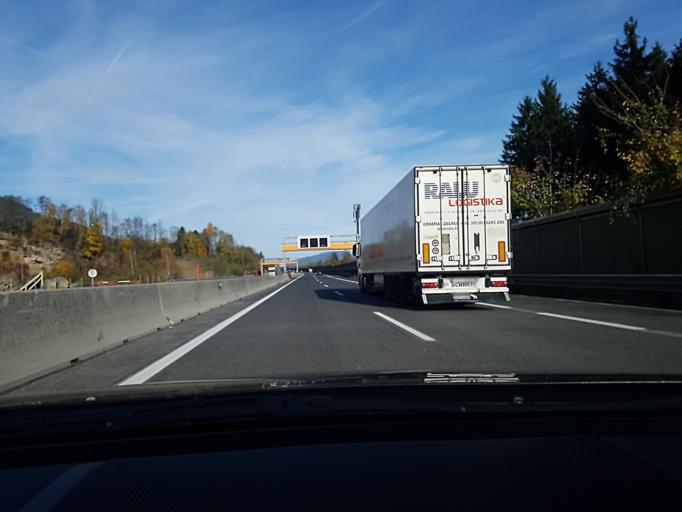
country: AT
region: Salzburg
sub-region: Politischer Bezirk Hallein
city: Golling an der Salzach
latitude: 47.5949
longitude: 13.1518
